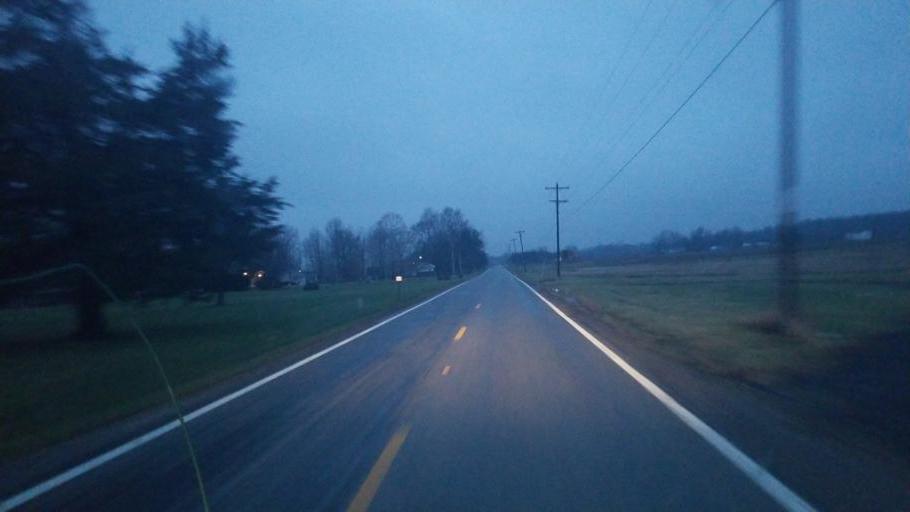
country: US
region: Ohio
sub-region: Morrow County
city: Cardington
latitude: 40.4893
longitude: -82.8627
